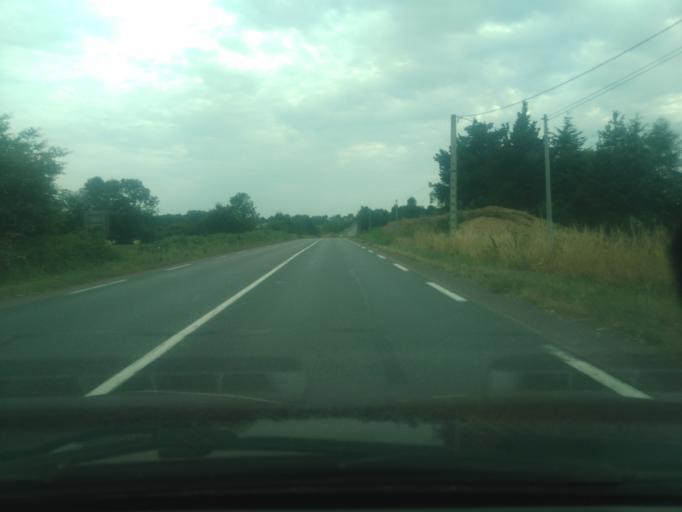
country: FR
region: Pays de la Loire
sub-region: Departement de la Vendee
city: Les Essarts
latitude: 46.7502
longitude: -1.2599
